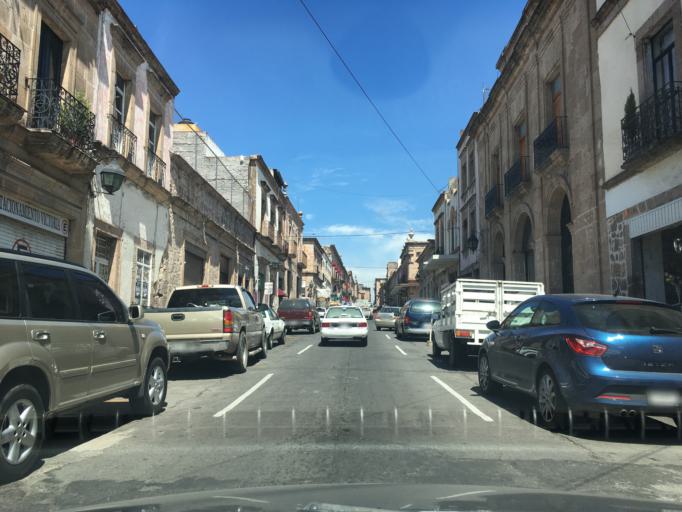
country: MX
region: Michoacan
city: Morelia
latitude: 19.6992
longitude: -101.1942
